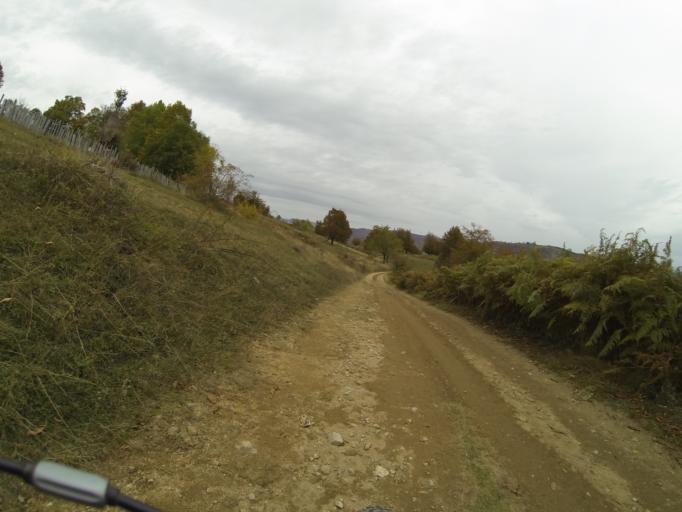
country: RO
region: Gorj
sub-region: Comuna Pades
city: Closani
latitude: 45.1171
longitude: 22.8505
